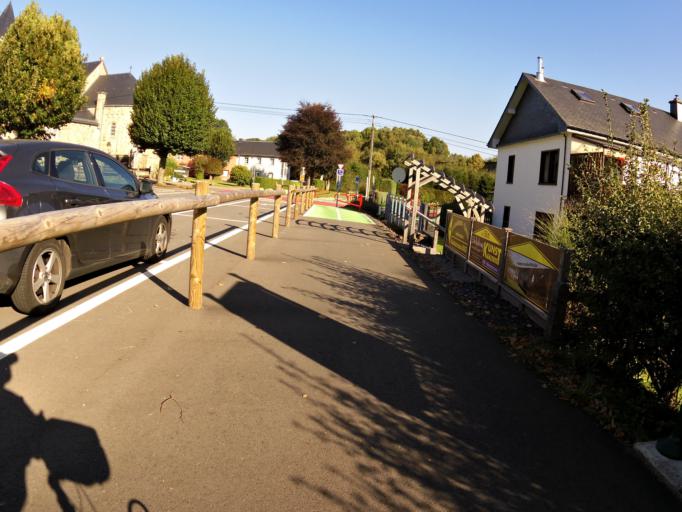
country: BE
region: Wallonia
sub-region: Province de Liege
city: Saint-Vith
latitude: 50.3328
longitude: 6.1177
